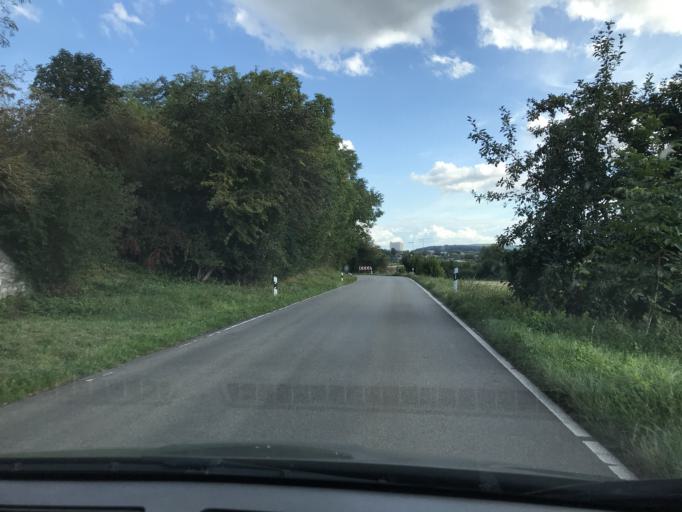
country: DE
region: Hesse
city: Gross-Umstadt
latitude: 49.8841
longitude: 8.9260
